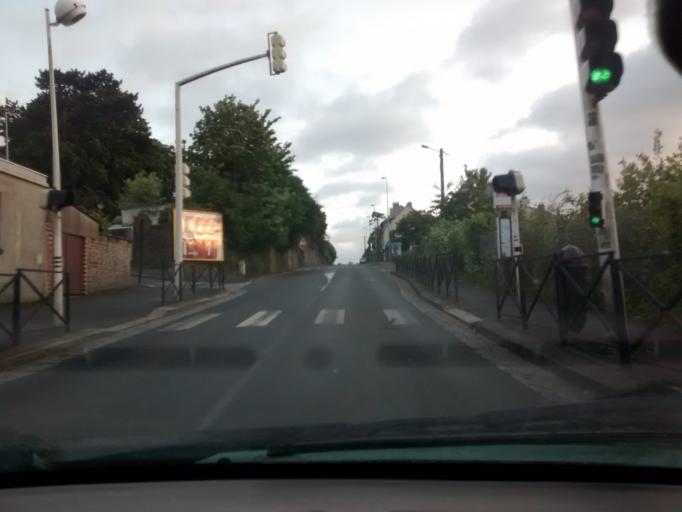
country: FR
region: Lower Normandy
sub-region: Departement de la Manche
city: Agneaux
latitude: 49.1120
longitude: -1.1016
